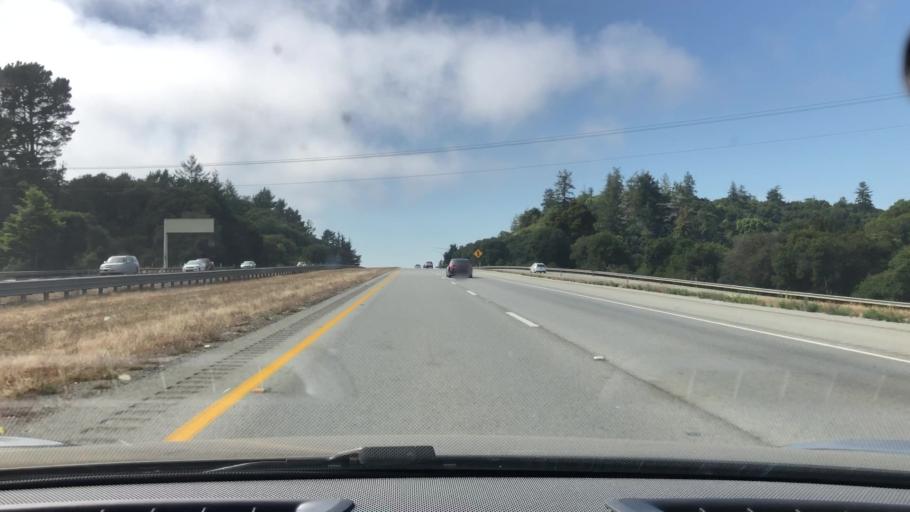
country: US
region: California
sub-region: Santa Cruz County
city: La Selva Beach
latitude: 36.9621
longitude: -121.8639
